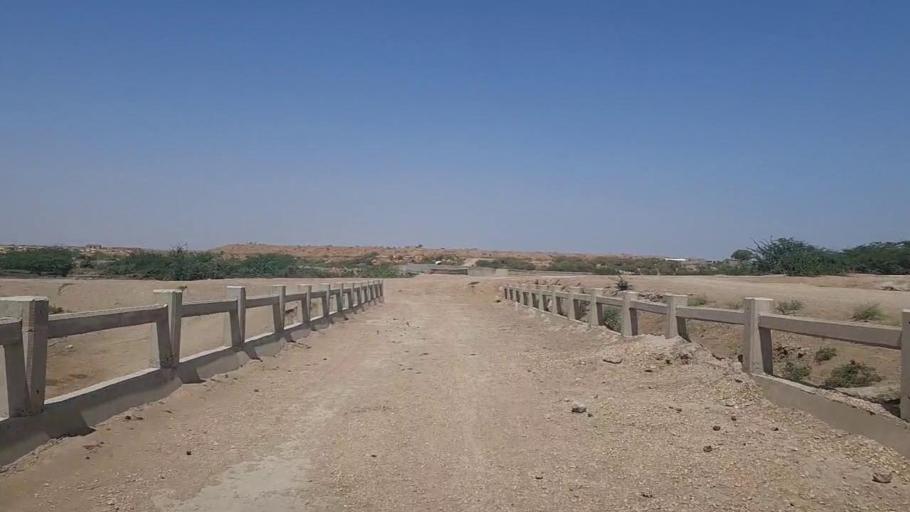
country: PK
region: Sindh
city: Thatta
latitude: 24.8153
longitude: 68.0059
